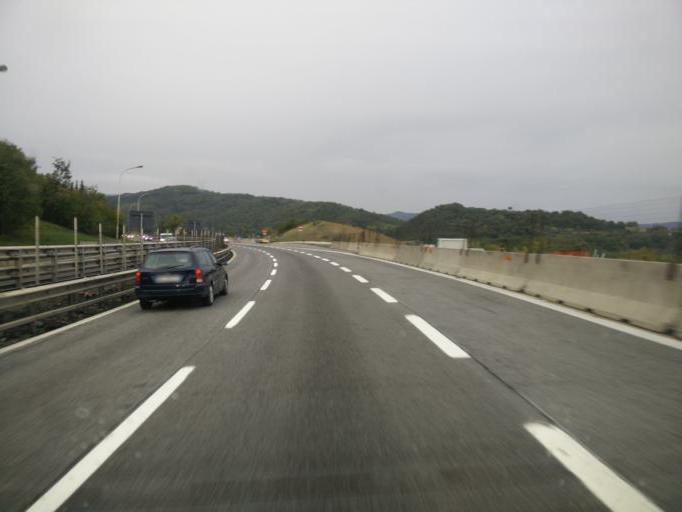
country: IT
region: Tuscany
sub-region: Province of Florence
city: Barberino di Mugello
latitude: 44.0307
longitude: 11.2259
